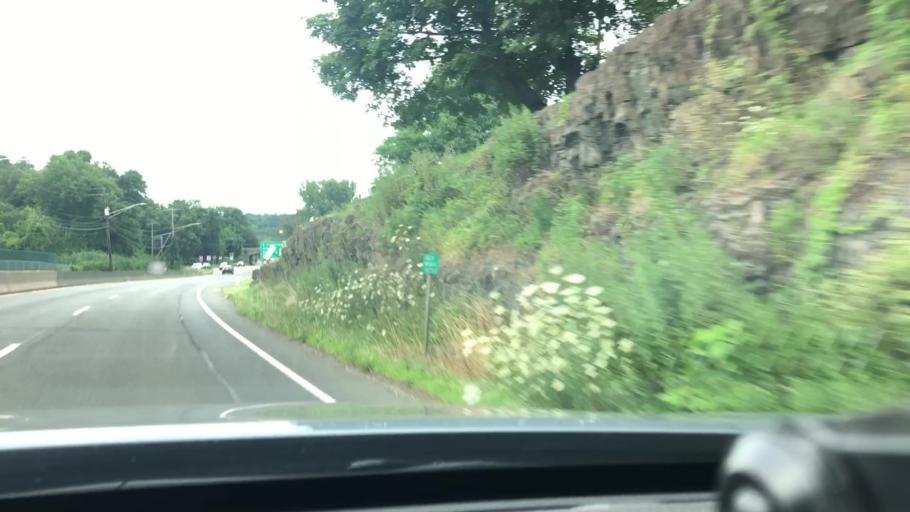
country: US
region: New York
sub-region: Rockland County
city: West Nyack
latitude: 41.0906
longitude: -73.9503
